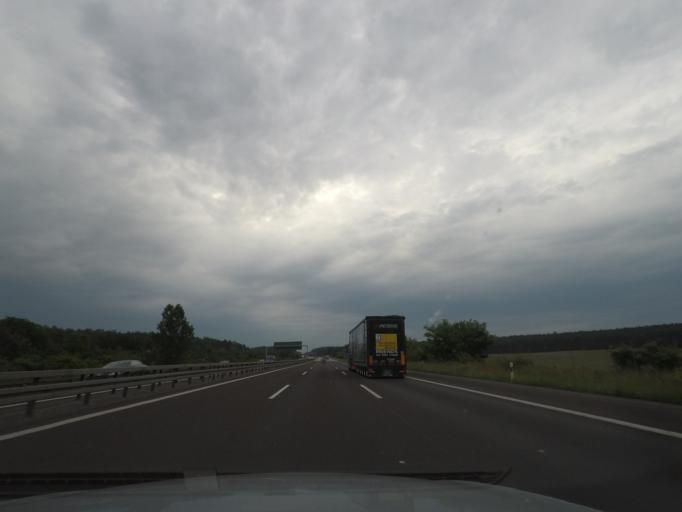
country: DE
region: Saxony-Anhalt
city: Hohenwarthe
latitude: 52.2225
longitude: 11.7241
